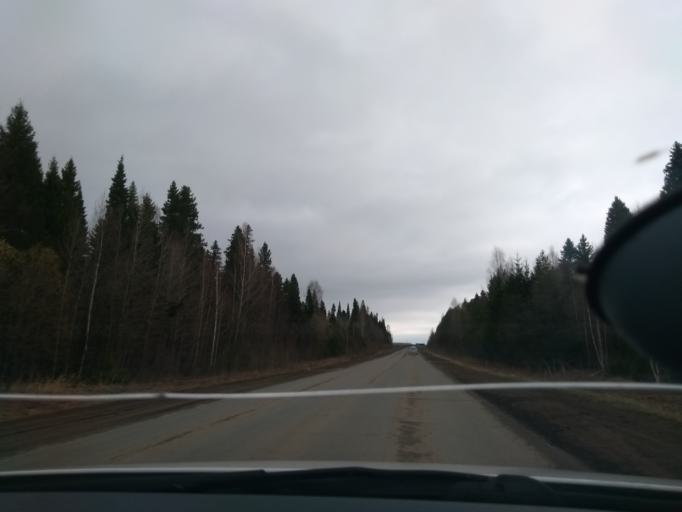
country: RU
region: Perm
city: Kungur
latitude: 57.3963
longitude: 56.8763
